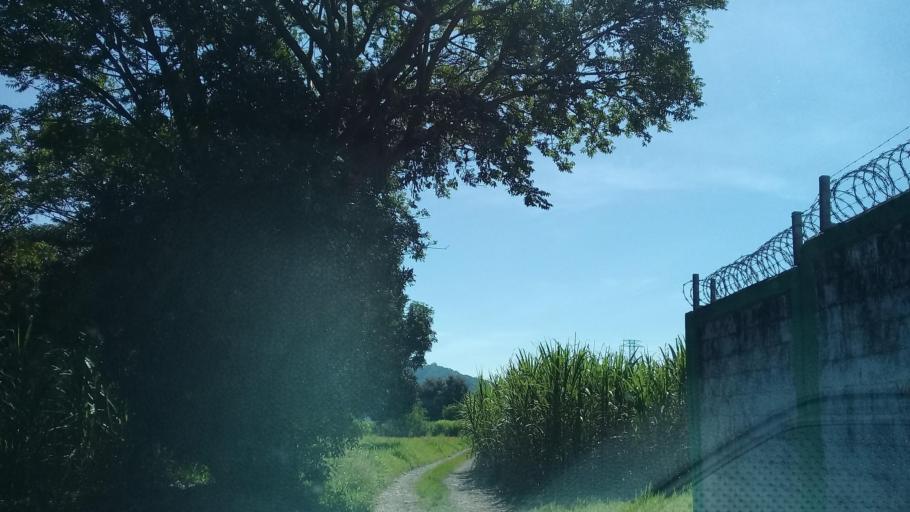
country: MX
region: Veracruz
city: Amatlan de los Reyes
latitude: 18.8582
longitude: -96.9012
